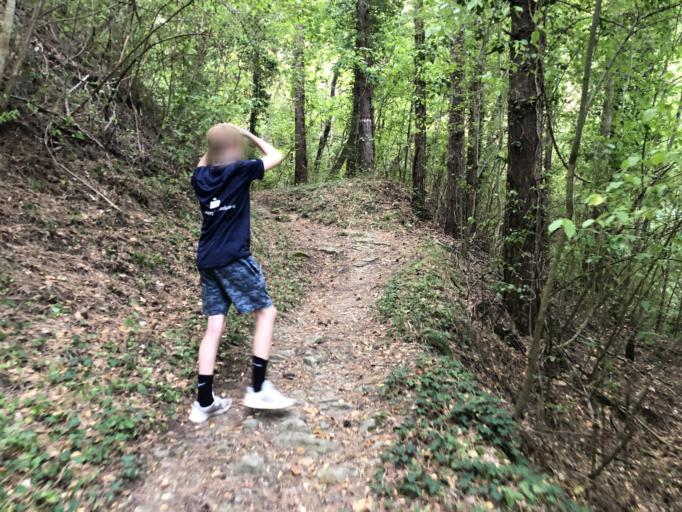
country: IT
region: Emilia-Romagna
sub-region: Forli-Cesena
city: Portico e San Benedetto
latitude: 44.0227
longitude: 11.7822
